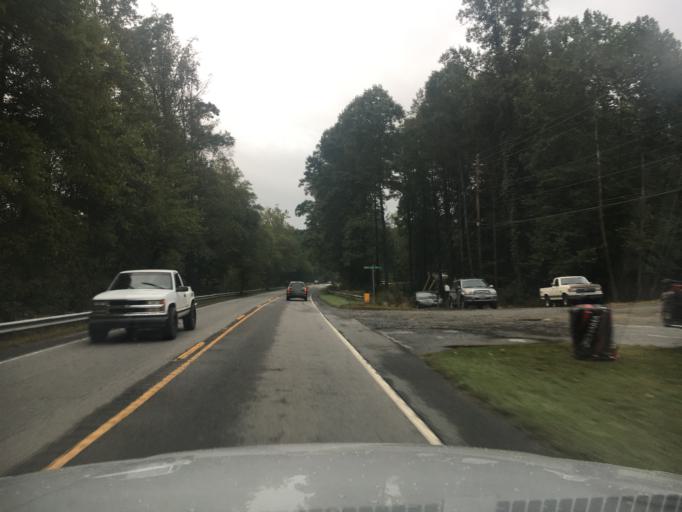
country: US
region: North Carolina
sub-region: Henderson County
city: Horse Shoe
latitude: 35.3366
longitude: -82.5666
